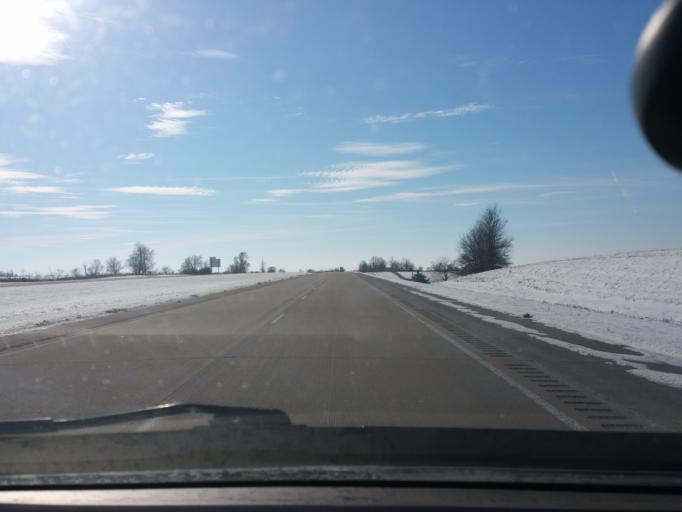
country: US
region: Iowa
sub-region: Decatur County
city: Leon
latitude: 40.8530
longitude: -93.8040
